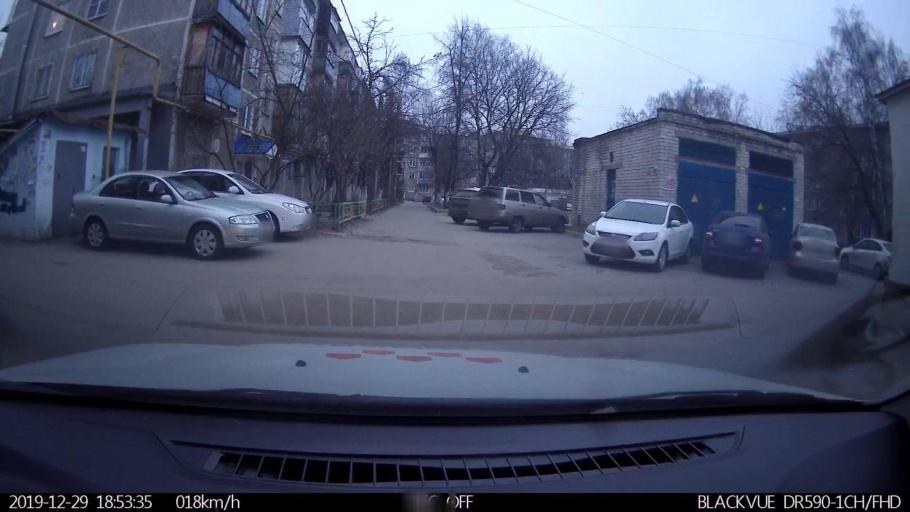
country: RU
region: Nizjnij Novgorod
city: Gorbatovka
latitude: 56.3474
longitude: 43.8520
